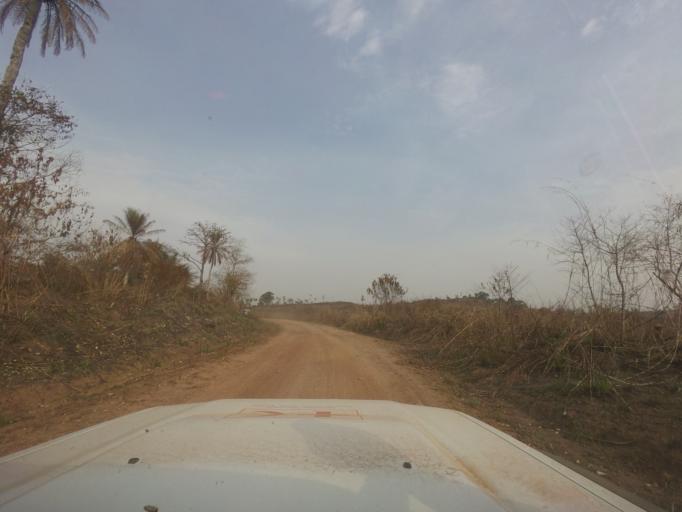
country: GN
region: Nzerekore
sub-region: Prefecture de Guekedou
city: Gueckedou
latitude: 8.5200
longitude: -10.2009
